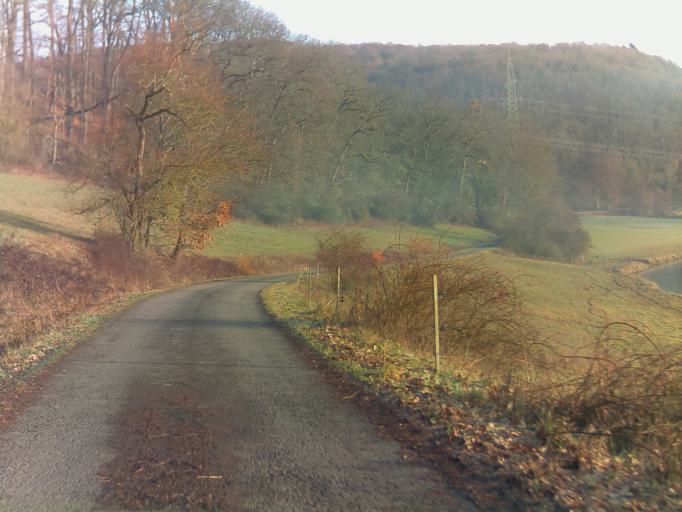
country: DE
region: Rheinland-Pfalz
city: Gries
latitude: 49.4219
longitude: 7.4094
